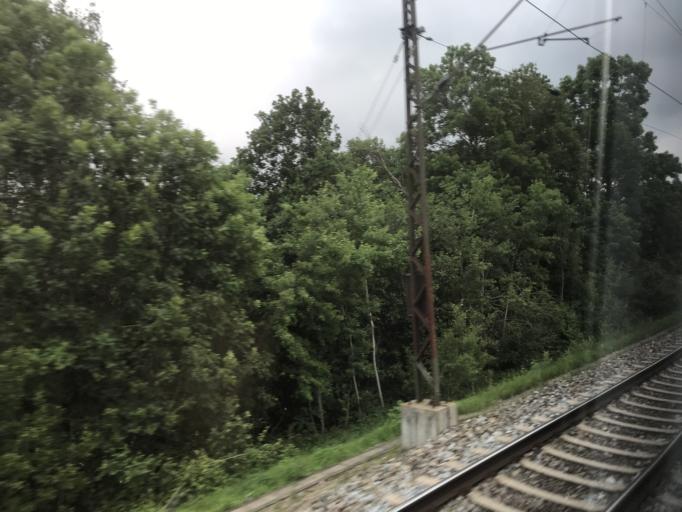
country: DE
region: Bavaria
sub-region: Swabia
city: Dinkelscherben
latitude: 48.3651
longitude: 10.5598
